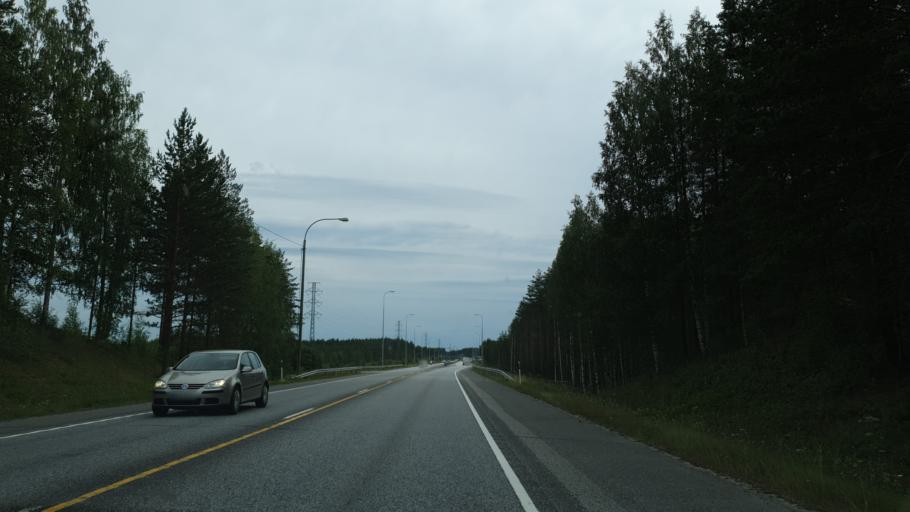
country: FI
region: North Karelia
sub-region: Joensuu
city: Joensuu
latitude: 62.6410
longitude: 29.7833
